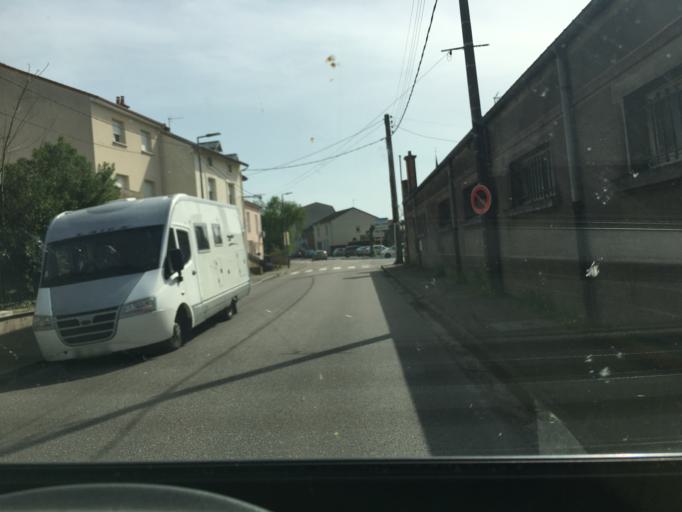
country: FR
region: Lorraine
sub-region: Departement de Meurthe-et-Moselle
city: Neuves-Maisons
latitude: 48.6163
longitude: 6.0988
